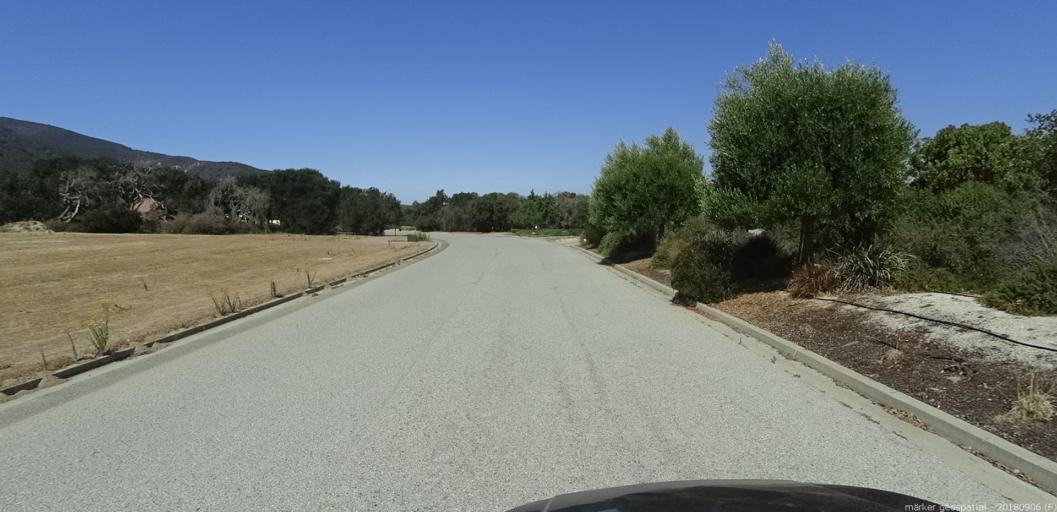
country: US
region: California
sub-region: Monterey County
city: Salinas
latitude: 36.5859
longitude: -121.6327
